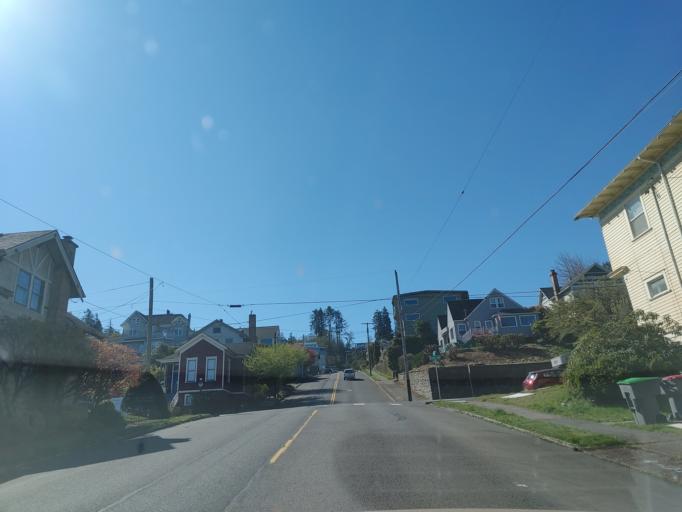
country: US
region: Oregon
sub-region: Clatsop County
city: Astoria
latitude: 46.1865
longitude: -123.8255
